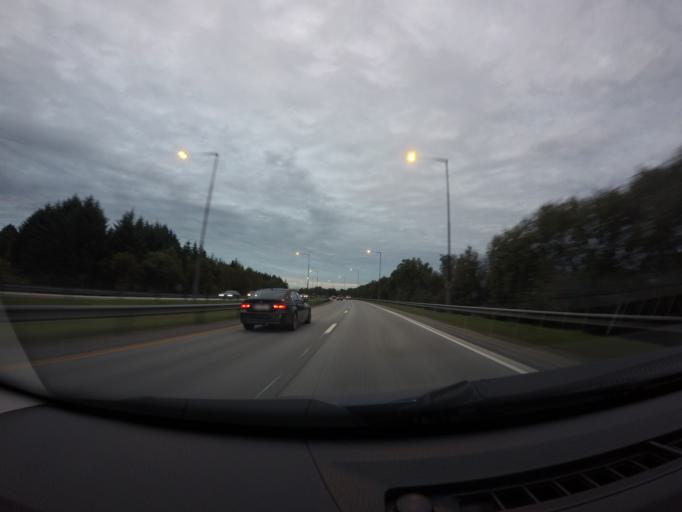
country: NO
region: Rogaland
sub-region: Stavanger
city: Stavanger
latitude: 58.9320
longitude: 5.7099
